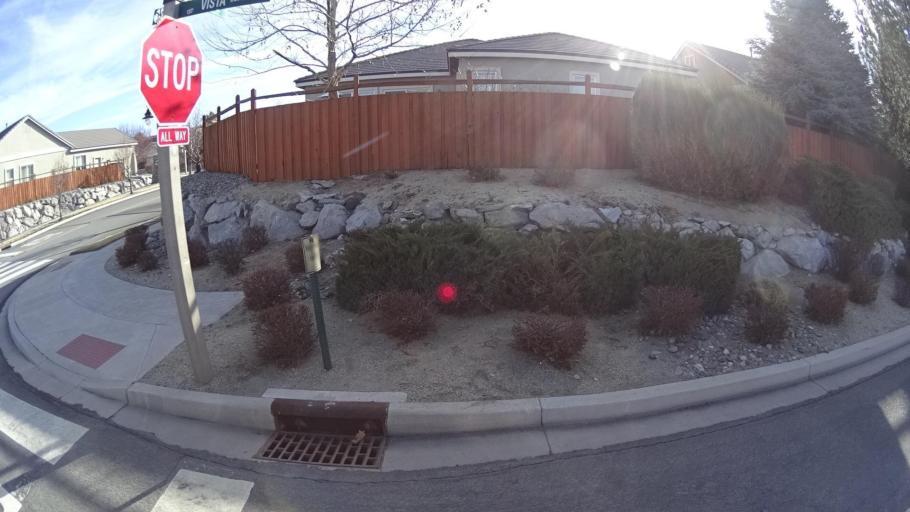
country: US
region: Nevada
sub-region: Washoe County
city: Spanish Springs
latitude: 39.6145
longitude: -119.6702
